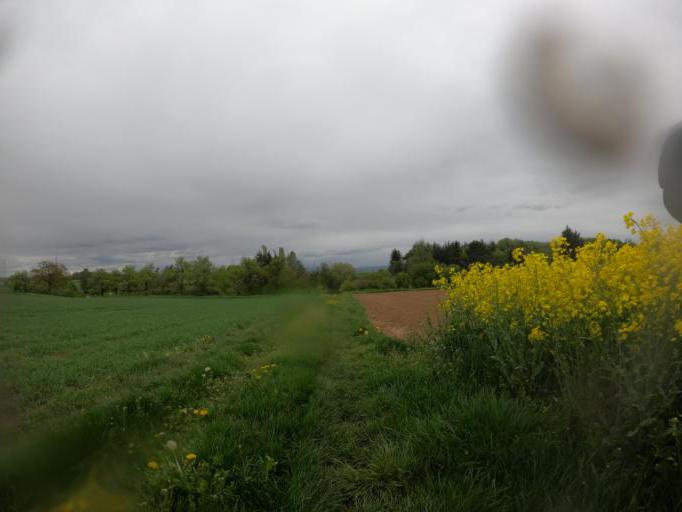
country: DE
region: Baden-Wuerttemberg
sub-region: Regierungsbezirk Stuttgart
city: Unterjettingen
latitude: 48.5613
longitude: 8.7919
